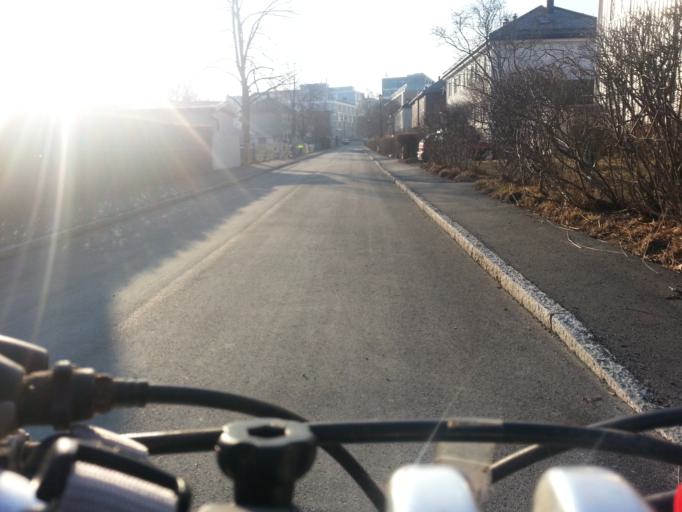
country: NO
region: Sor-Trondelag
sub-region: Trondheim
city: Trondheim
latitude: 63.4230
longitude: 10.3838
